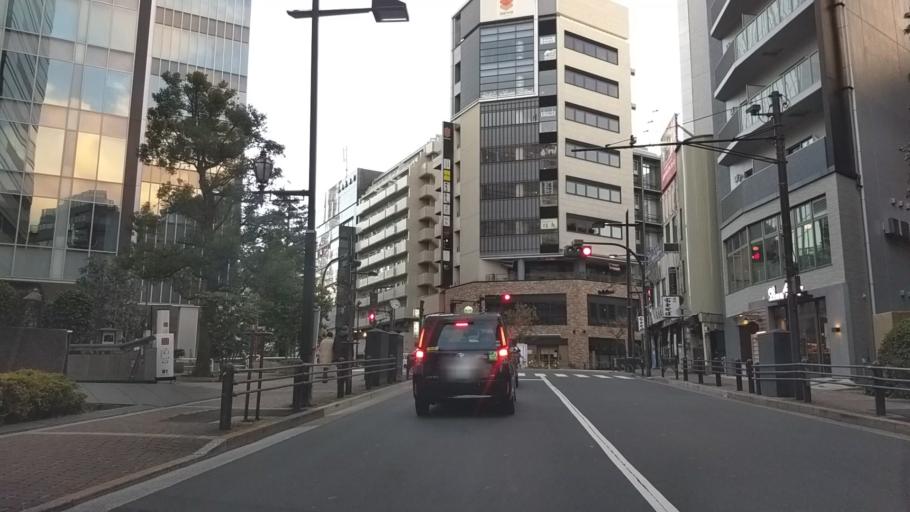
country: JP
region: Tokyo
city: Tokyo
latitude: 35.6898
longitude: 139.7355
